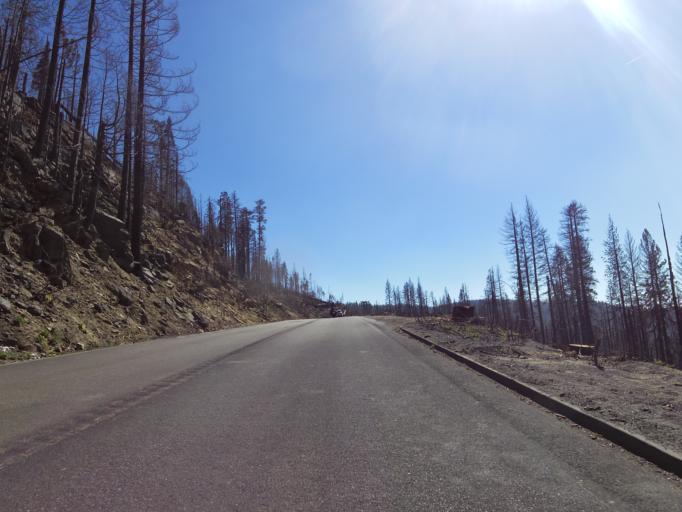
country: US
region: California
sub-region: Mariposa County
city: Yosemite Valley
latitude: 37.6621
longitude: -119.7103
